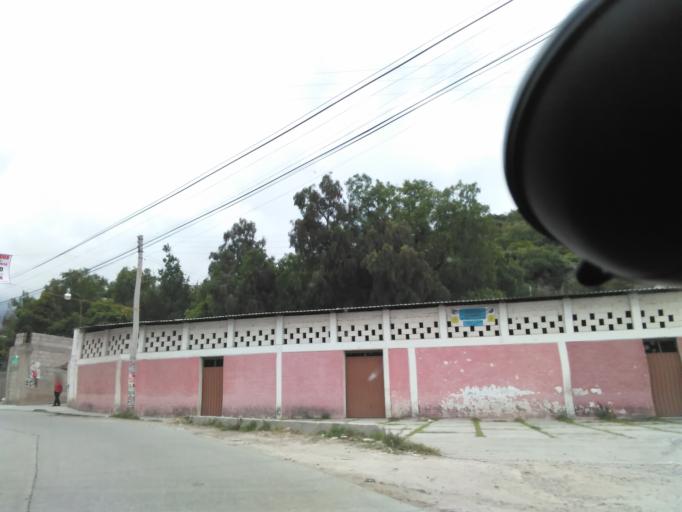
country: MX
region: Hidalgo
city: Tula de Allende
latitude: 20.0602
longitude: -99.3488
